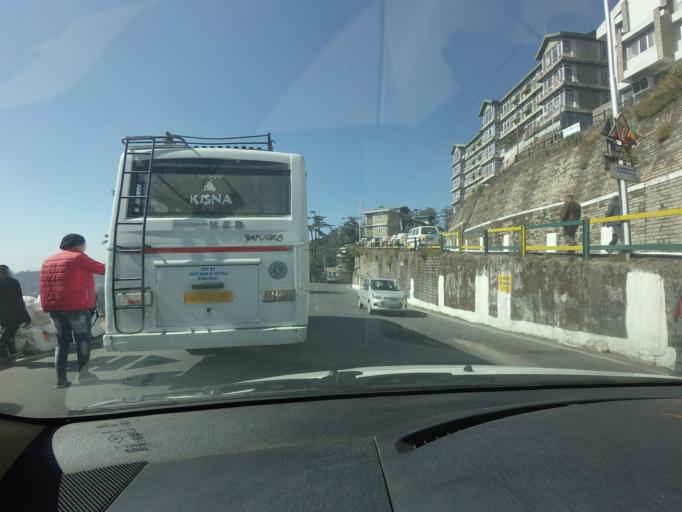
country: IN
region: Himachal Pradesh
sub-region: Shimla
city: Shimla
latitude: 31.1028
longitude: 77.1602
